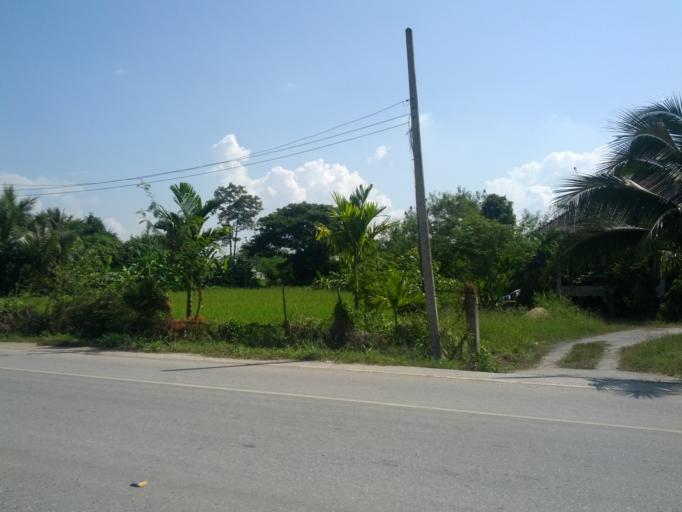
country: TH
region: Chiang Mai
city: San Kamphaeng
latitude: 18.7982
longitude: 99.1085
